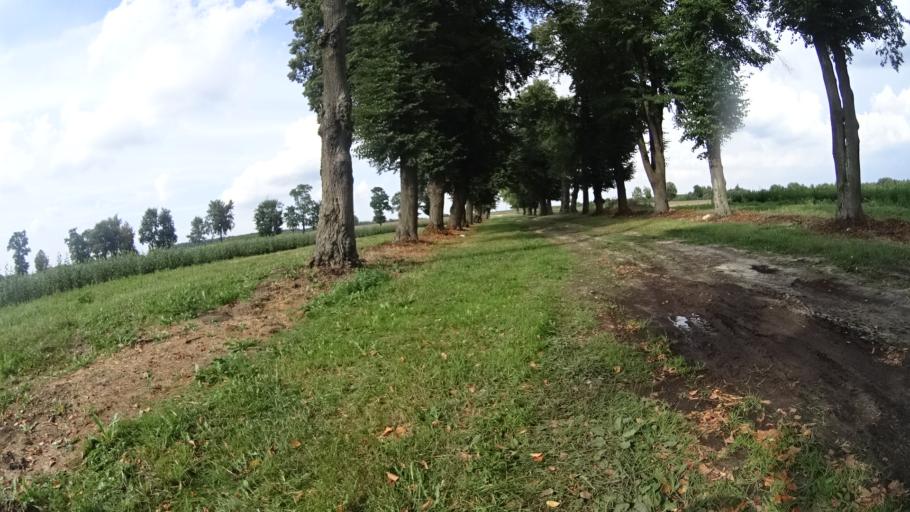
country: PL
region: Masovian Voivodeship
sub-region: Powiat grojecki
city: Goszczyn
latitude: 51.6941
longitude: 20.8234
